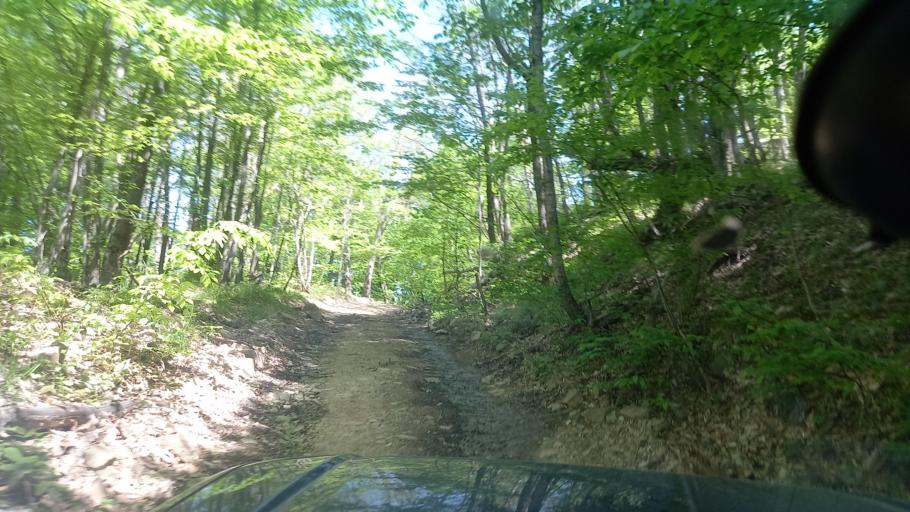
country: RU
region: Krasnodarskiy
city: Tuapse
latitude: 44.2552
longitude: 39.2840
